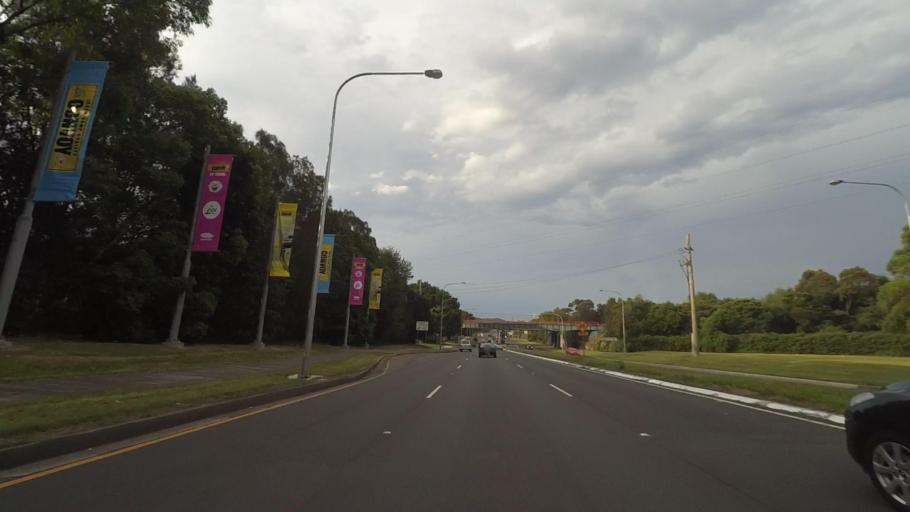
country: AU
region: New South Wales
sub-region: Wollongong
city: Cringila
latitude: -34.4640
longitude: 150.8717
